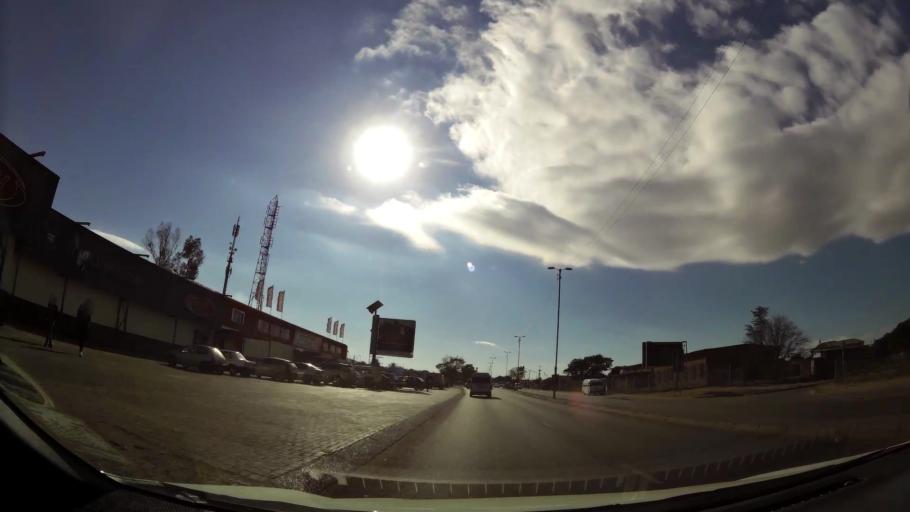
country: ZA
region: Gauteng
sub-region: City of Tshwane Metropolitan Municipality
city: Cullinan
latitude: -25.7124
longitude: 28.3777
